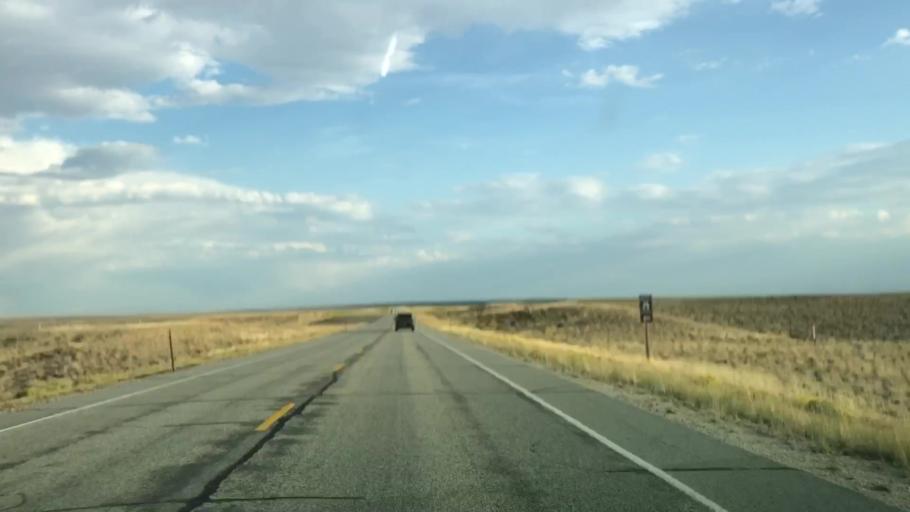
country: US
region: Wyoming
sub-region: Sublette County
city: Marbleton
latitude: 42.3298
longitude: -109.5152
